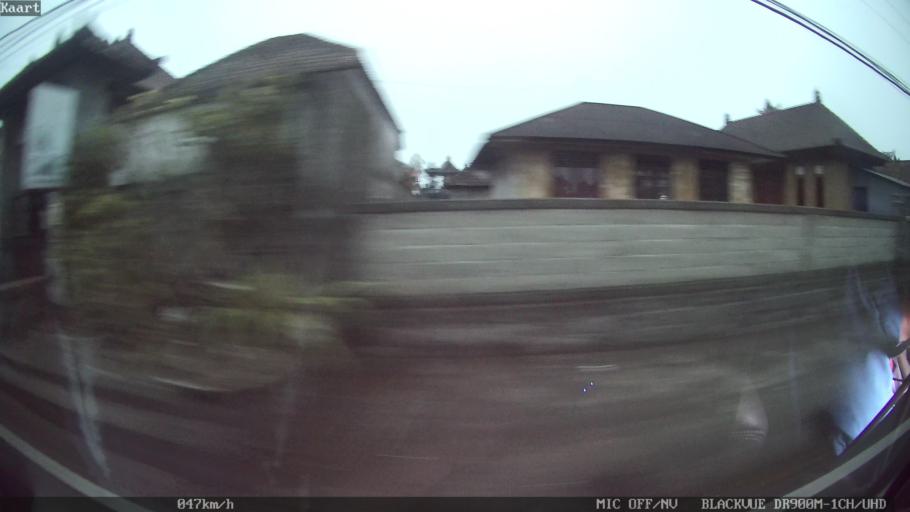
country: ID
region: Bali
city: Banjar Taro Kelod
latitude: -8.3106
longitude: 115.3044
